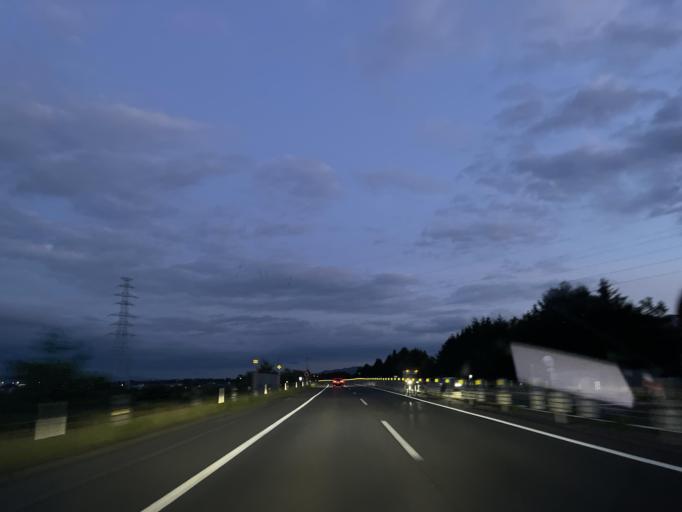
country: JP
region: Iwate
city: Morioka-shi
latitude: 39.6853
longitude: 141.1025
